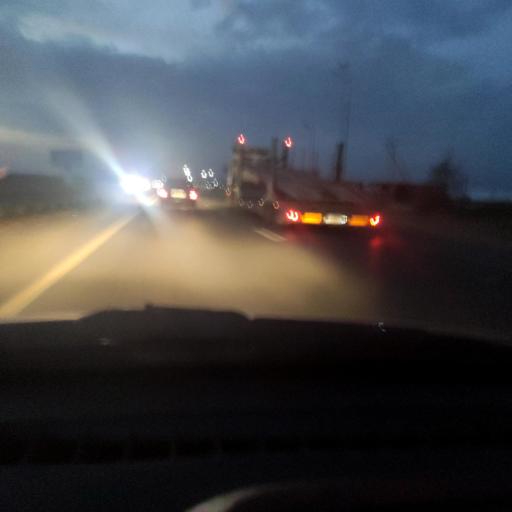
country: RU
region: Samara
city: Zhigulevsk
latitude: 53.5531
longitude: 49.5053
